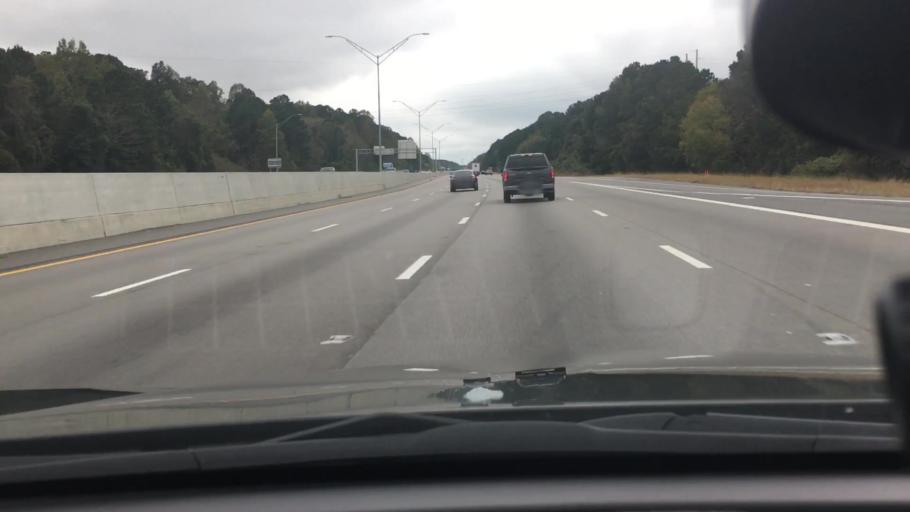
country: US
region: North Carolina
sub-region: Wake County
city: West Raleigh
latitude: 35.7571
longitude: -78.6692
